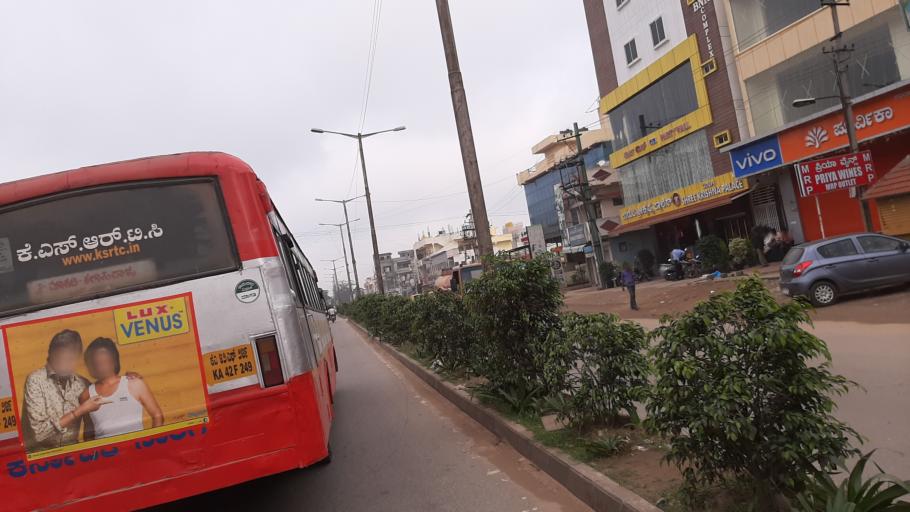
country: IN
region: Karnataka
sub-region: Bangalore Urban
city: Bangalore
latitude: 12.9872
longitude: 77.4757
